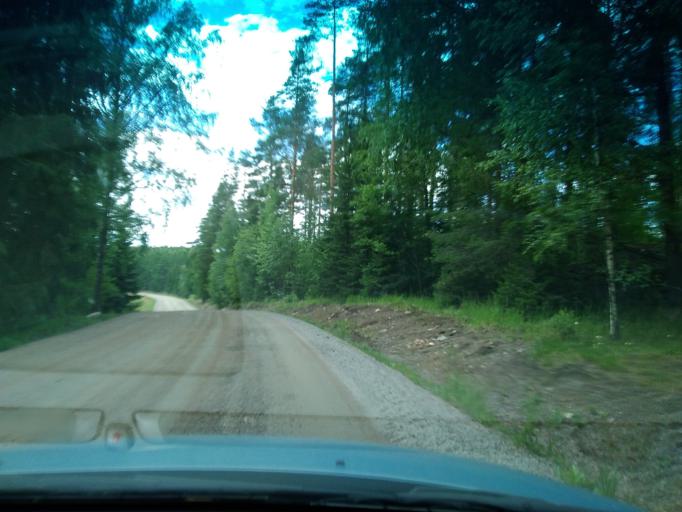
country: FI
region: Central Finland
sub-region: Saarijaervi-Viitasaari
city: Karstula
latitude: 62.8007
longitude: 24.9877
